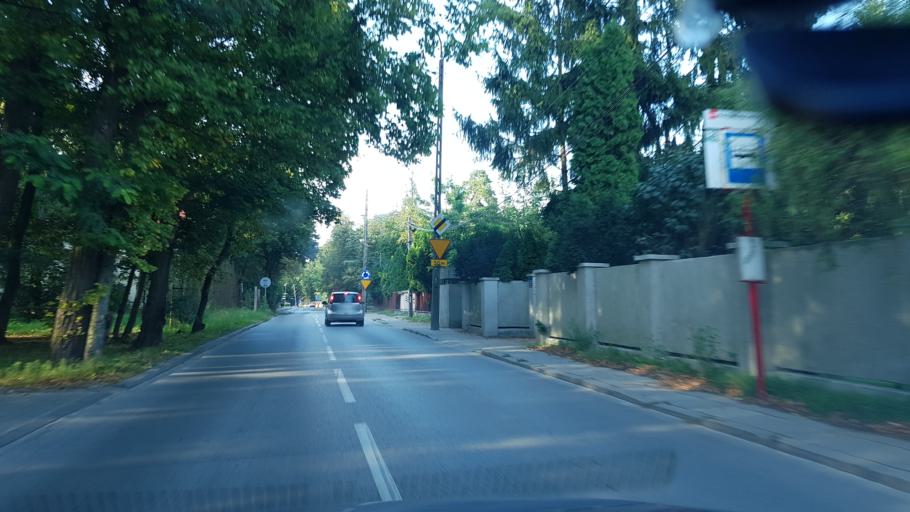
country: PL
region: Masovian Voivodeship
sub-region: Powiat piaseczynski
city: Konstancin-Jeziorna
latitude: 52.0763
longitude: 21.0985
